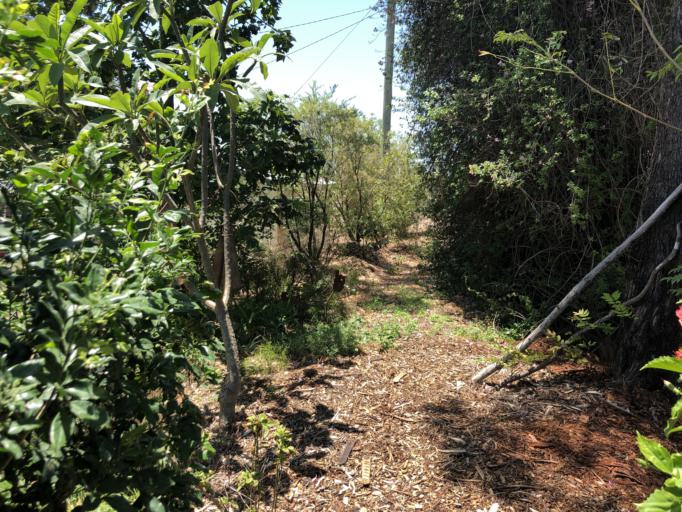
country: AU
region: Queensland
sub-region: Lockyer Valley
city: Gatton
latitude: -27.5875
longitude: 152.3452
